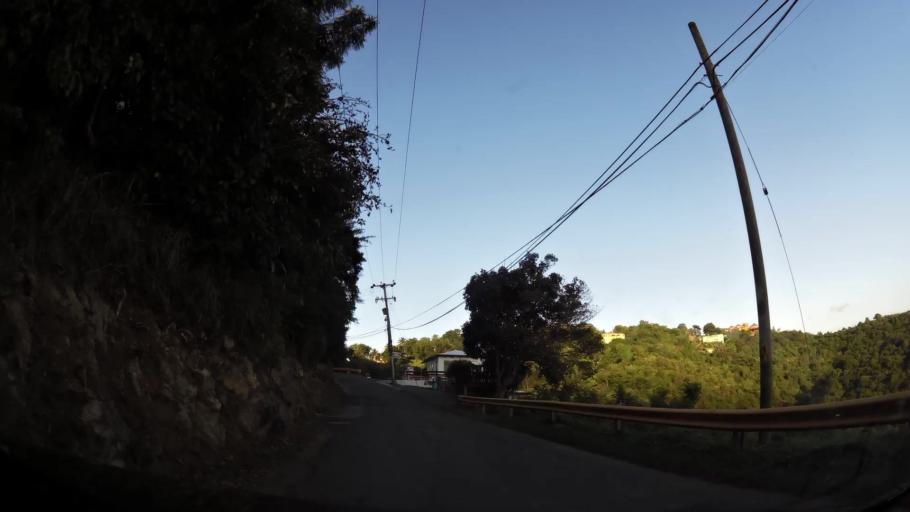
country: VG
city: Road Town
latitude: 18.4396
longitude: -64.6283
